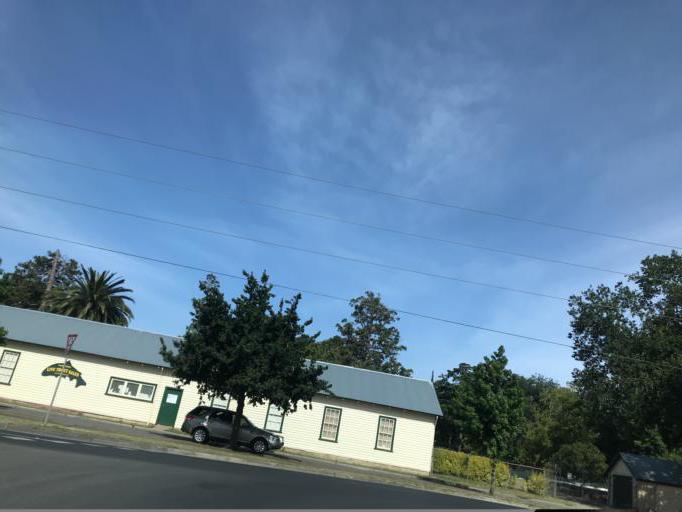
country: AU
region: Victoria
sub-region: Ballarat North
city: Newington
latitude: -37.5505
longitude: 143.8200
